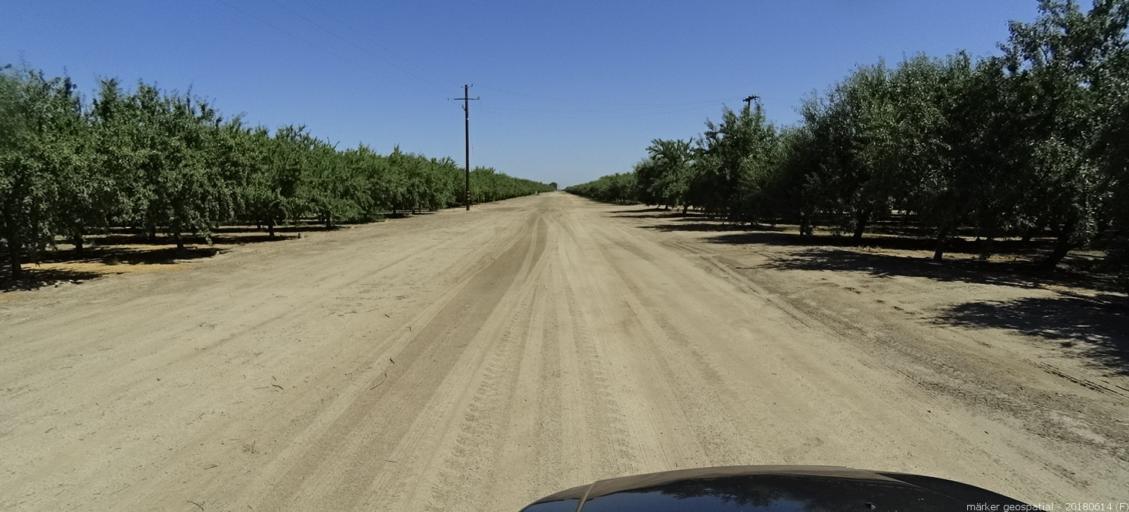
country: US
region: California
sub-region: Madera County
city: Fairmead
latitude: 36.9304
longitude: -120.2242
